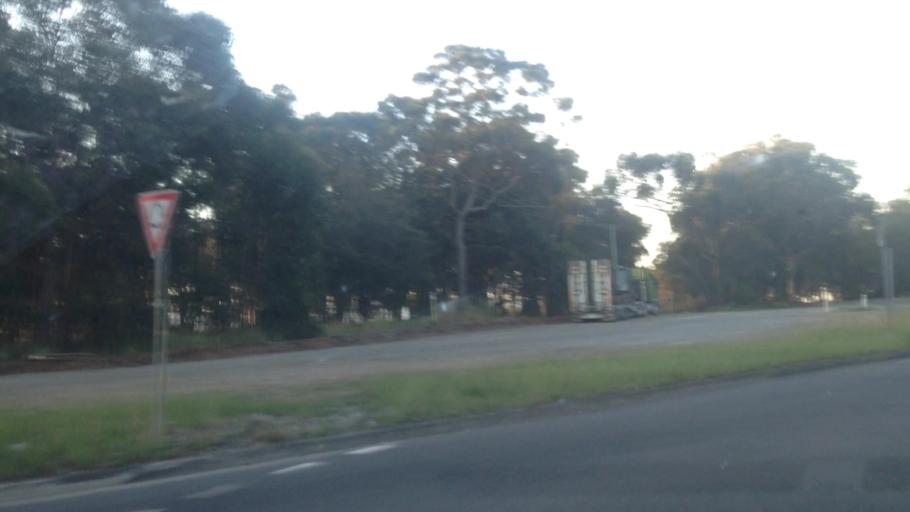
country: AU
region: New South Wales
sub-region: Lake Macquarie Shire
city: Dora Creek
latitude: -33.1129
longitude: 151.4780
